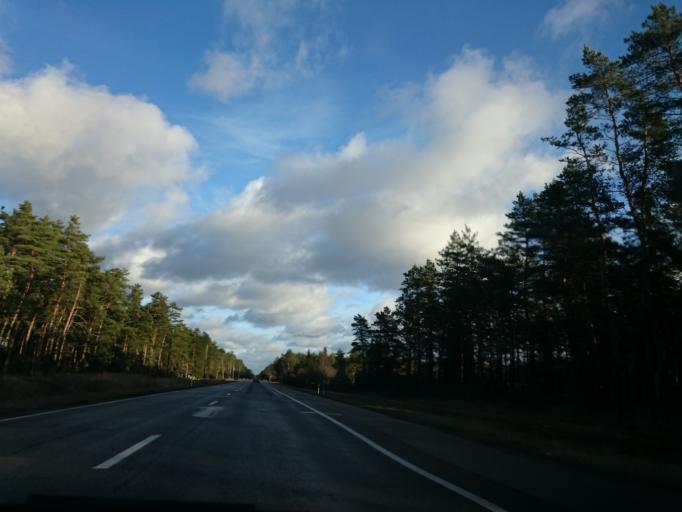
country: LV
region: Incukalns
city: Vangazi
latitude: 57.0680
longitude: 24.4870
